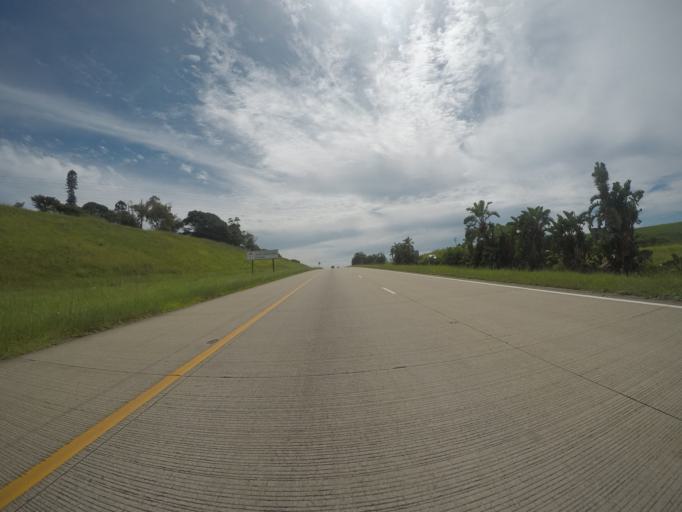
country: ZA
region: KwaZulu-Natal
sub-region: iLembe District Municipality
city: Stanger
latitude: -29.3448
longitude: 31.3254
